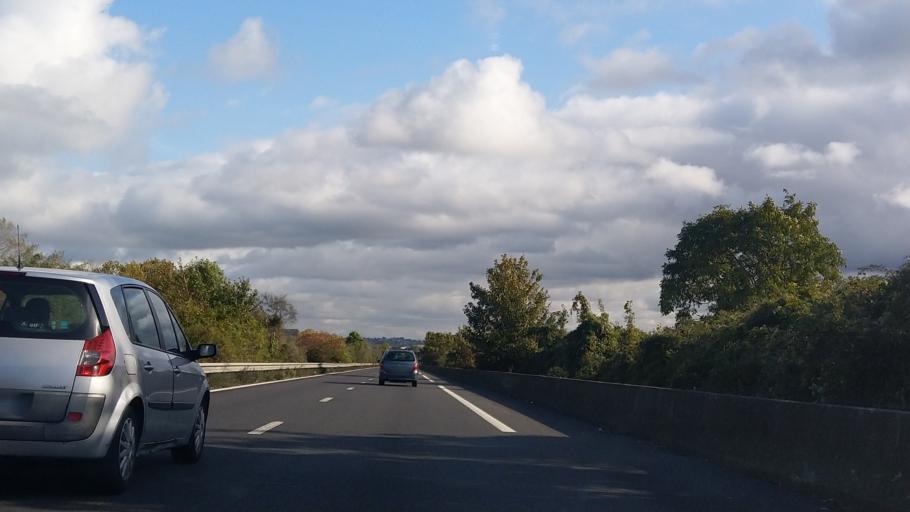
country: FR
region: Ile-de-France
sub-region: Departement du Val-d'Oise
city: Le Plessis-Bouchard
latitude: 49.0094
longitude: 2.2335
